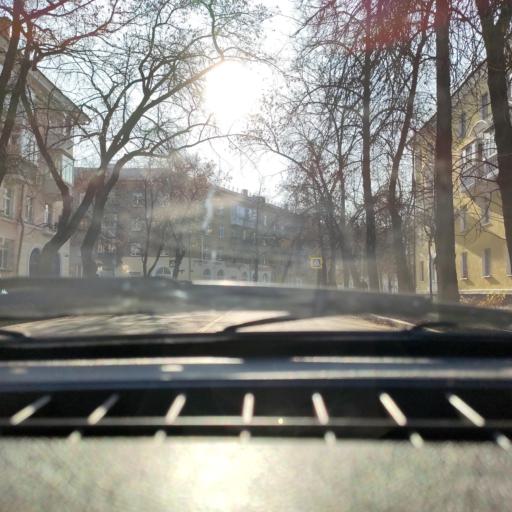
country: RU
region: Bashkortostan
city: Ufa
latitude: 54.8209
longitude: 56.0710
